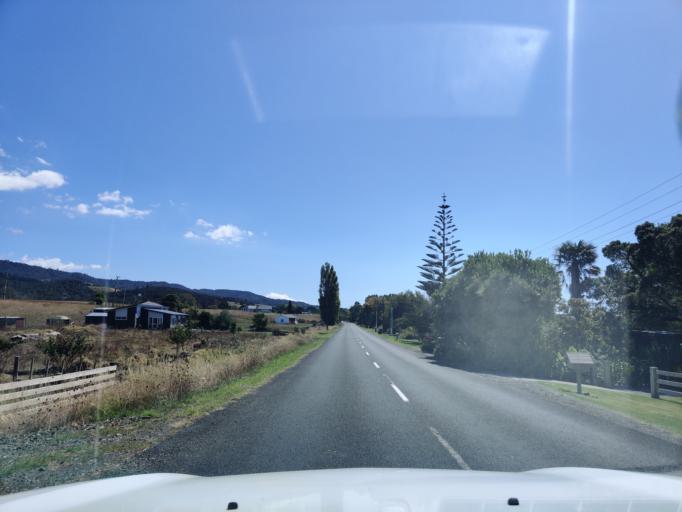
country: NZ
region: Waikato
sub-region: Thames-Coromandel District
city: Thames
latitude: -37.0477
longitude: 175.2992
